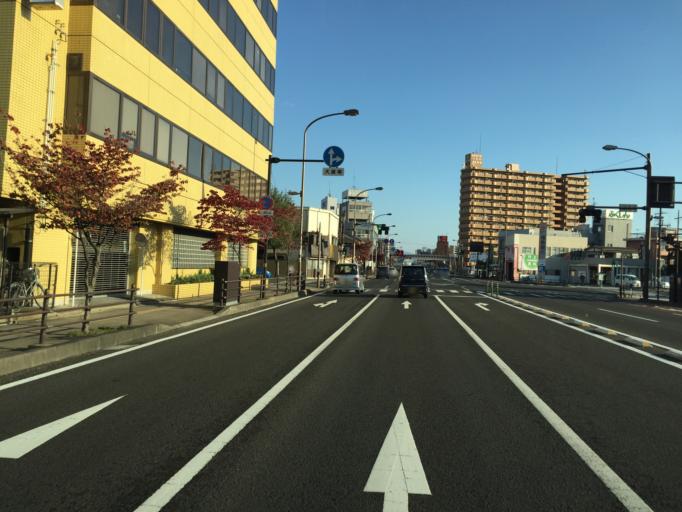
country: JP
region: Fukushima
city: Fukushima-shi
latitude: 37.7562
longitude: 140.4732
